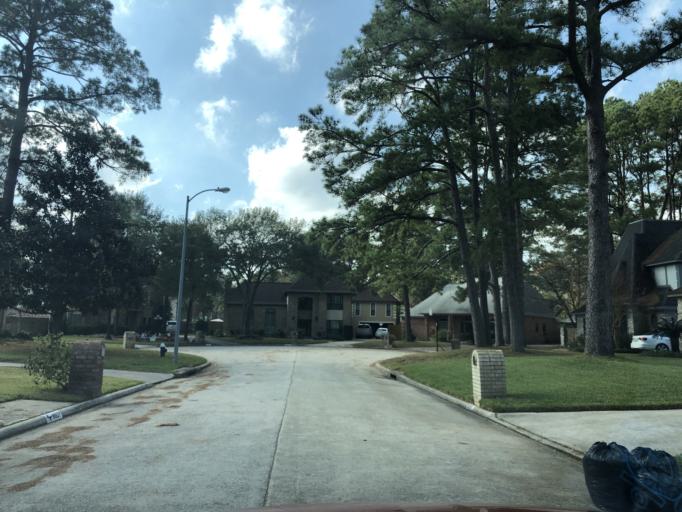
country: US
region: Texas
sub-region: Harris County
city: Tomball
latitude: 30.0299
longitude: -95.5463
